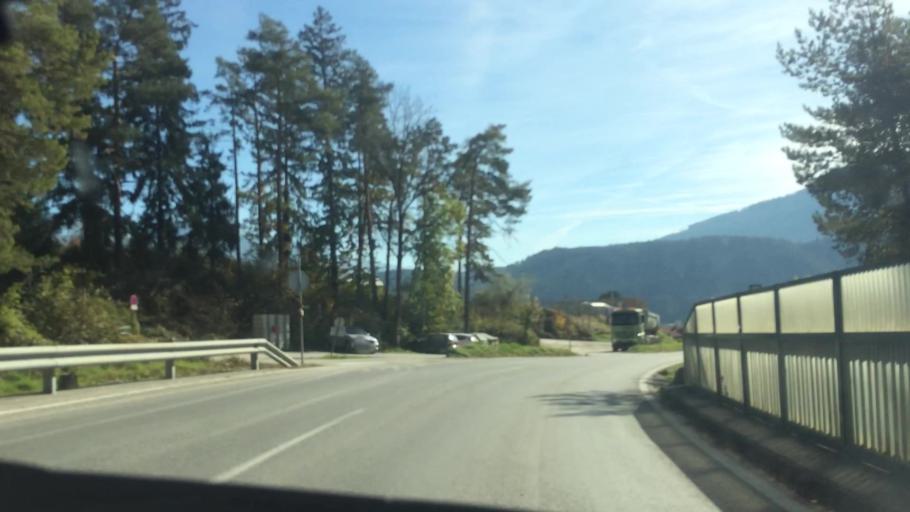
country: AT
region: Tyrol
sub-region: Politischer Bezirk Innsbruck Land
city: Vols
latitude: 47.2654
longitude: 11.3243
